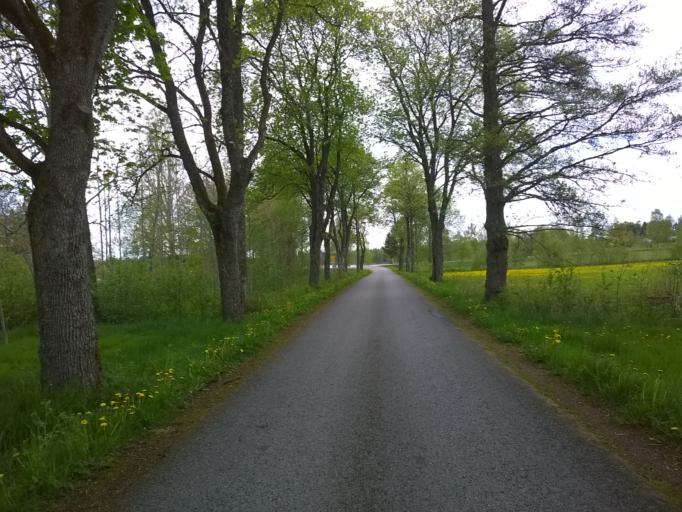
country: SE
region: Joenkoeping
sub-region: Eksjo Kommun
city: Eksjoe
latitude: 57.6456
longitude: 14.9806
